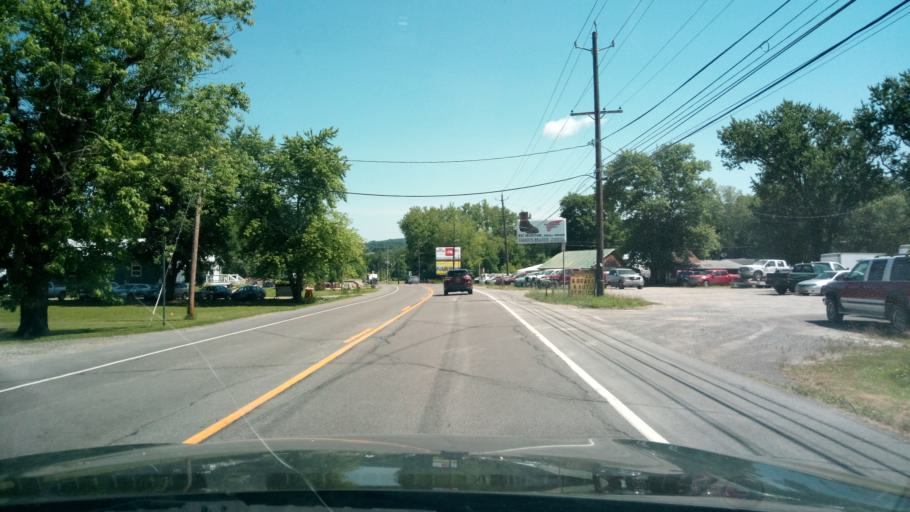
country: US
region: New York
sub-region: Schuyler County
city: Montour Falls
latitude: 42.3316
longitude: -76.8385
